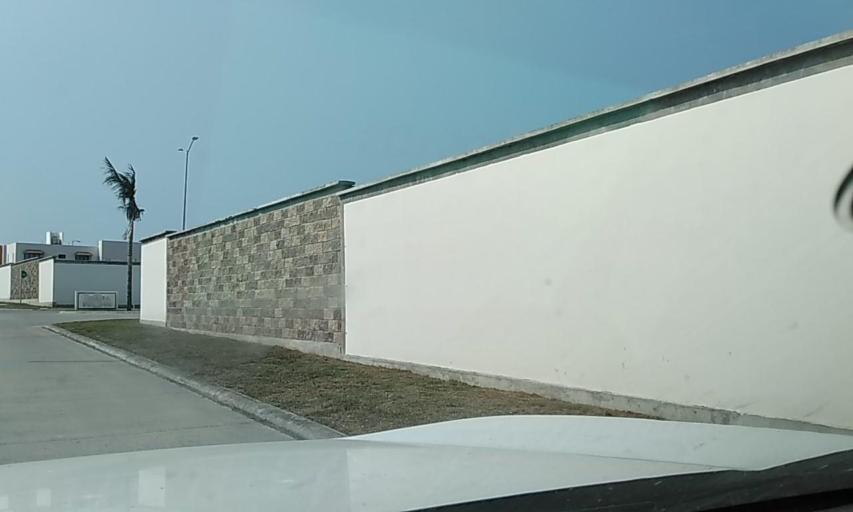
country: MX
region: Veracruz
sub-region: Alvarado
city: Playa de la Libertad
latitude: 19.0411
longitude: -96.0601
